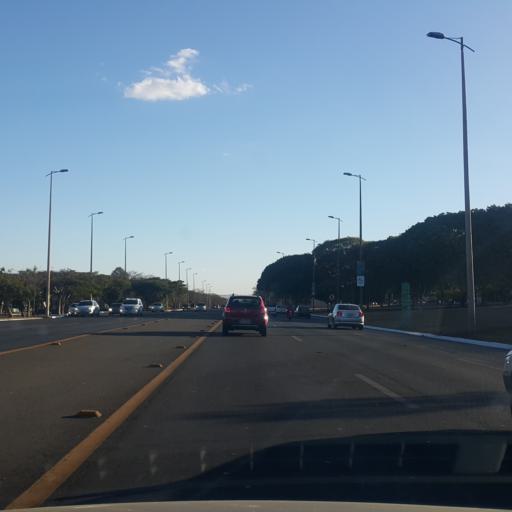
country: BR
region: Federal District
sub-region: Brasilia
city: Brasilia
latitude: -15.8174
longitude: -47.9013
